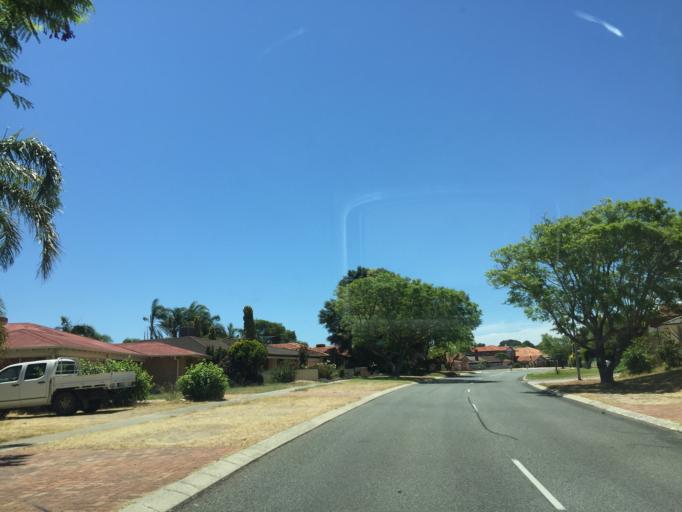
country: AU
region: Western Australia
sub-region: Melville
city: Winthrop
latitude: -32.0619
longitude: 115.8358
